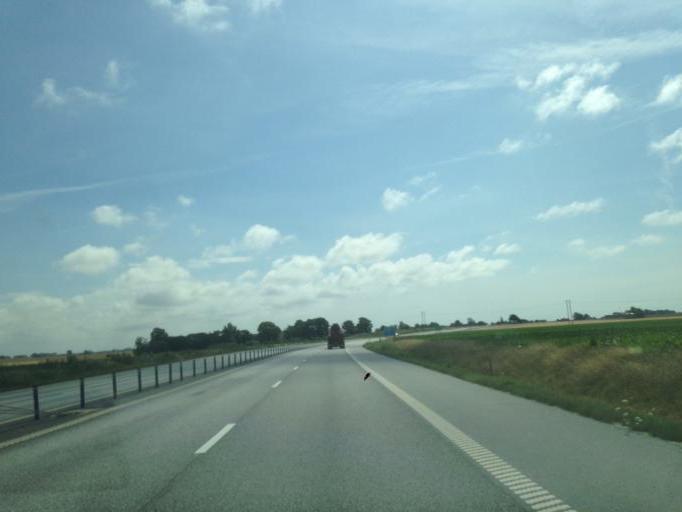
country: SE
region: Skane
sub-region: Trelleborgs Kommun
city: Skare
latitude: 55.4233
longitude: 13.0571
